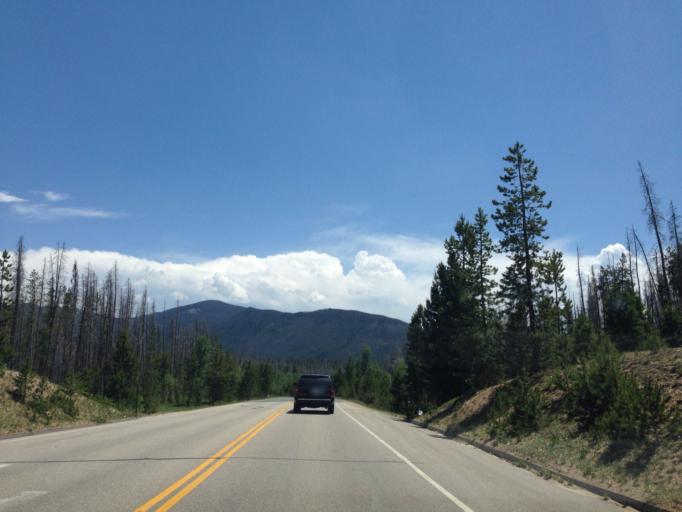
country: US
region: Colorado
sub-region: Grand County
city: Granby
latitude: 40.2650
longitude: -105.8327
